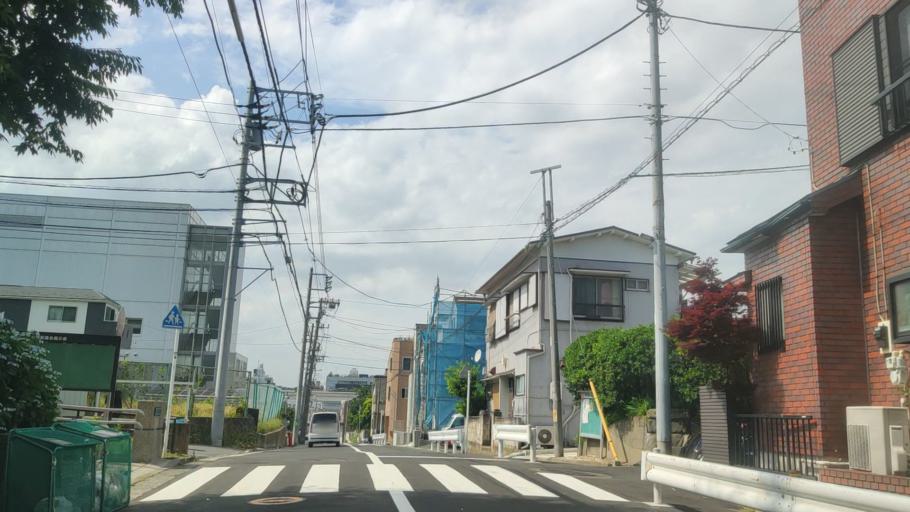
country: JP
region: Kanagawa
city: Yokohama
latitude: 35.4308
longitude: 139.6290
